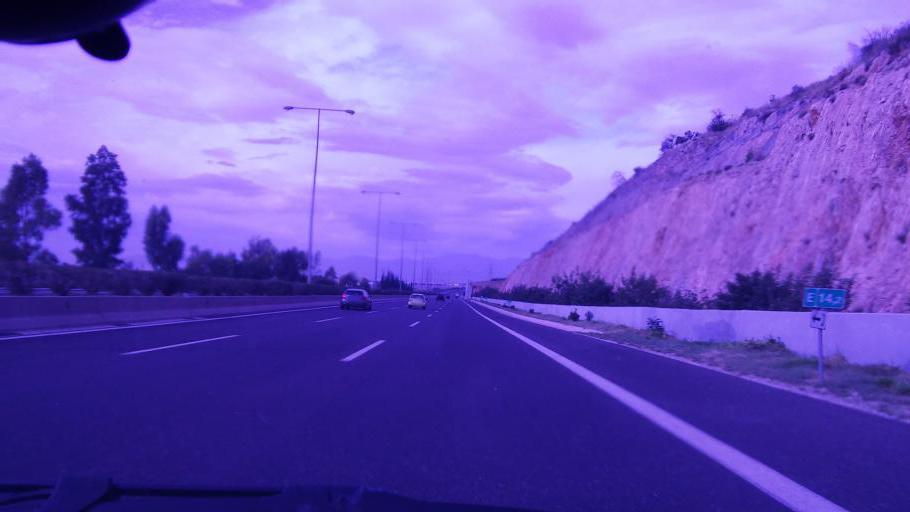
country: GR
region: Attica
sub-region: Nomarchia Dytikis Attikis
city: Fyli
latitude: 38.0866
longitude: 23.6547
